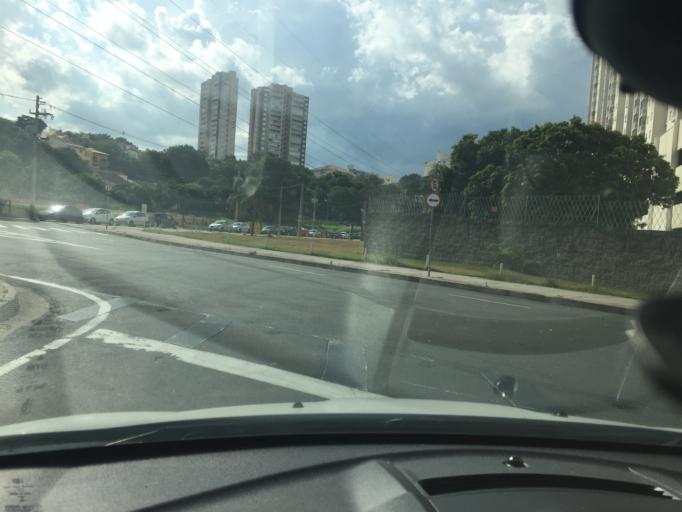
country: BR
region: Sao Paulo
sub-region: Jundiai
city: Jundiai
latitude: -23.1819
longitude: -46.9056
